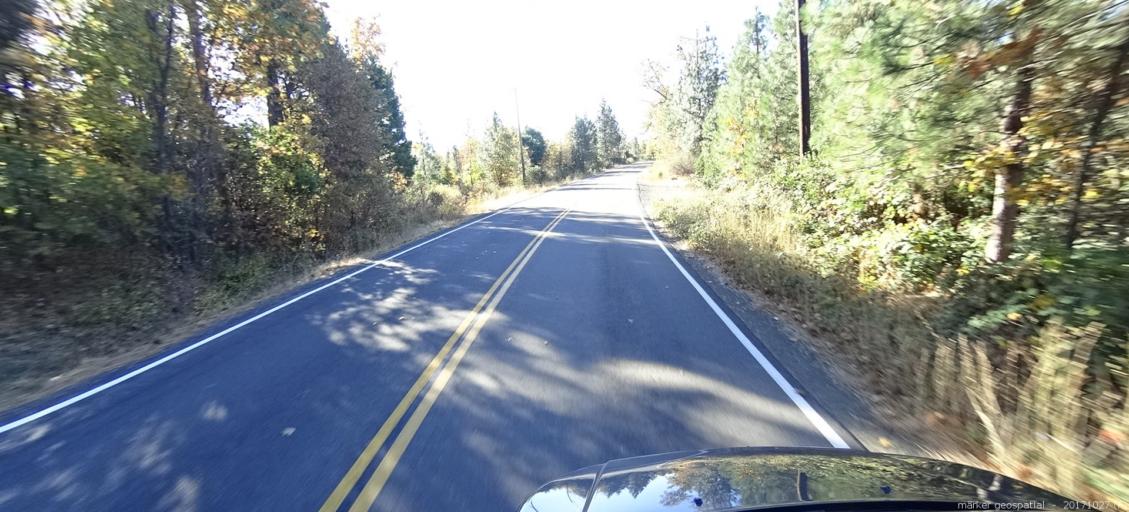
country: US
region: California
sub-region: Shasta County
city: Burney
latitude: 40.8819
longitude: -121.9081
